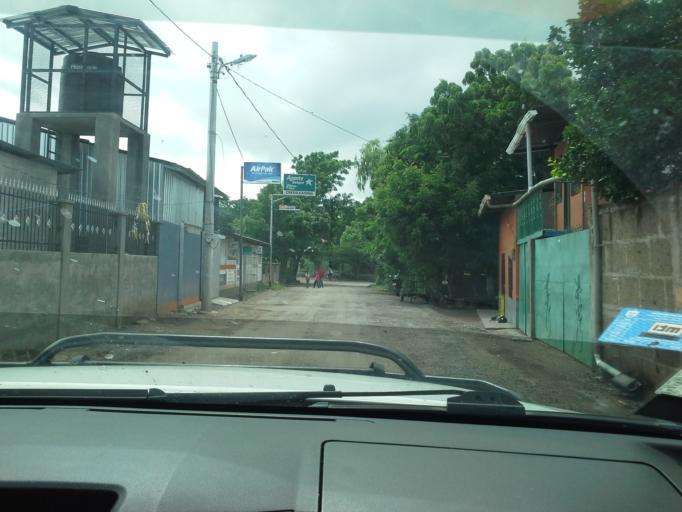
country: NI
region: Matagalpa
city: Ciudad Dario
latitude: 12.8372
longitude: -86.2168
